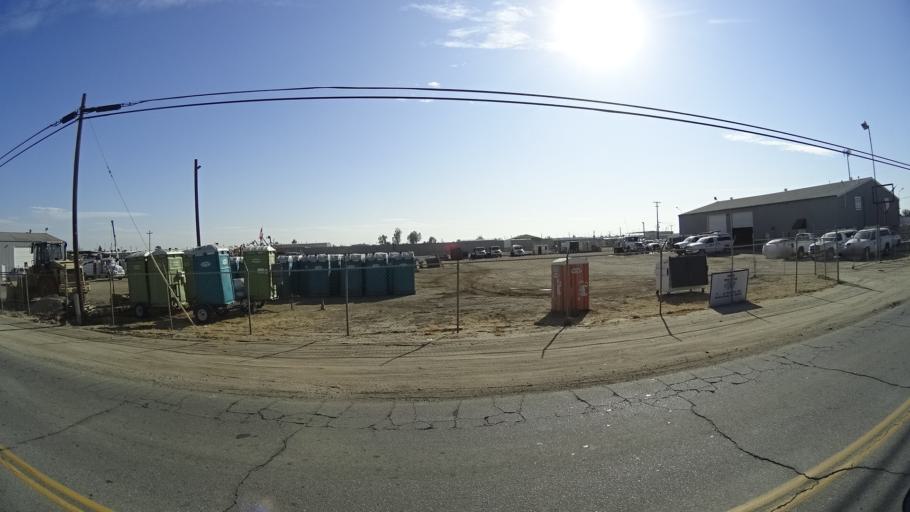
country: US
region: California
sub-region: Kern County
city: Greenacres
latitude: 35.3906
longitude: -119.0862
